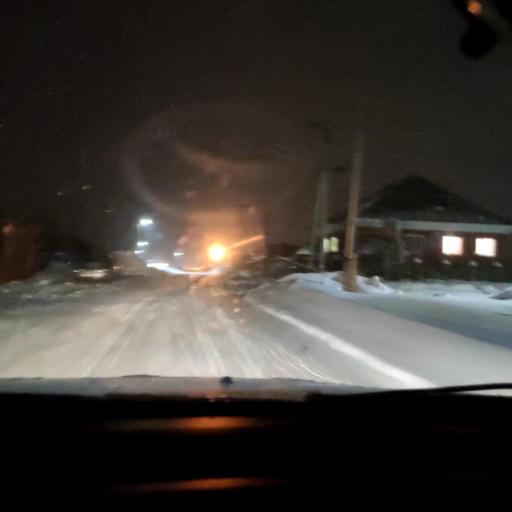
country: RU
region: Bashkortostan
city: Iglino
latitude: 54.8267
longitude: 56.3825
